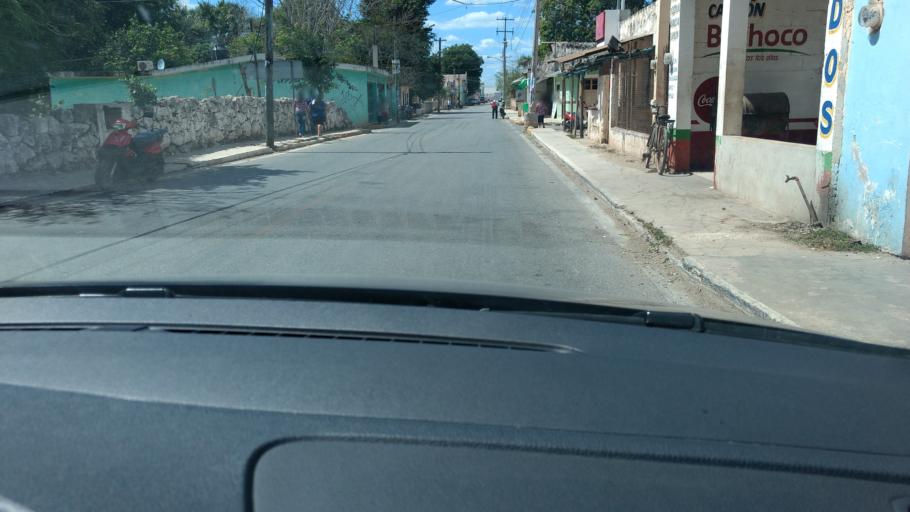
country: MX
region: Yucatan
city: Tzucacab
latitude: 20.0720
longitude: -89.0466
